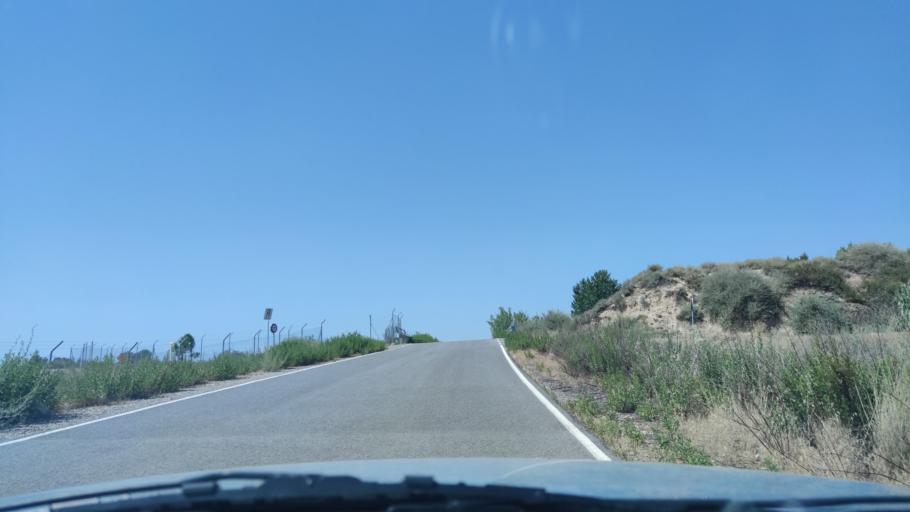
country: ES
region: Catalonia
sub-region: Provincia de Lleida
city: Alpicat
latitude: 41.6572
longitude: 0.5796
